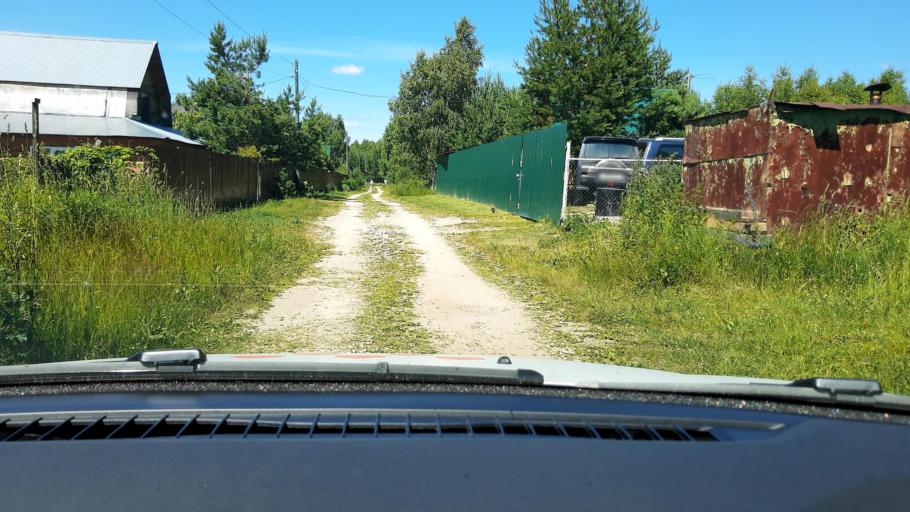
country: RU
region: Nizjnij Novgorod
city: Surovatikha
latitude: 55.8682
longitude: 43.9646
